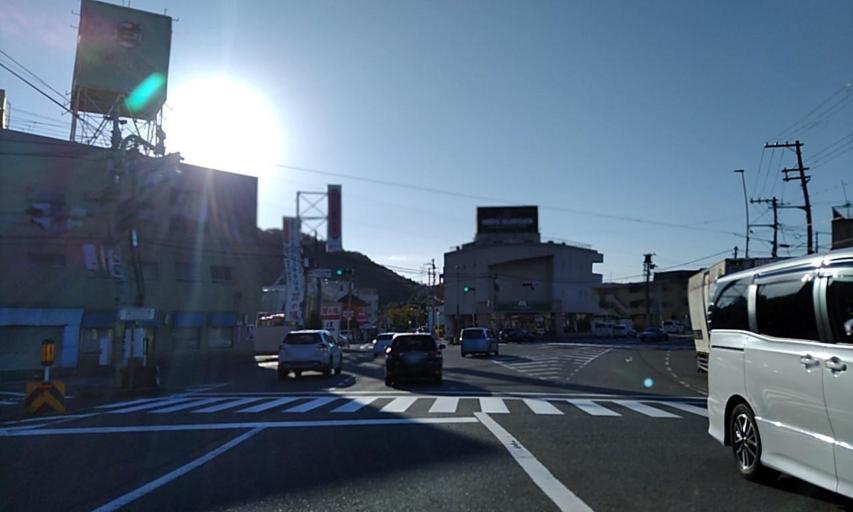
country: JP
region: Wakayama
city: Kainan
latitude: 34.1852
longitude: 135.1855
